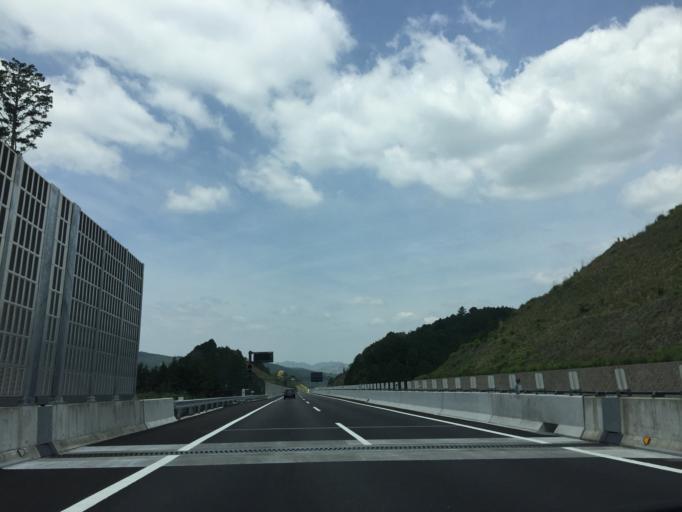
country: JP
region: Aichi
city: Shinshiro
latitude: 34.8974
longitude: 137.6249
